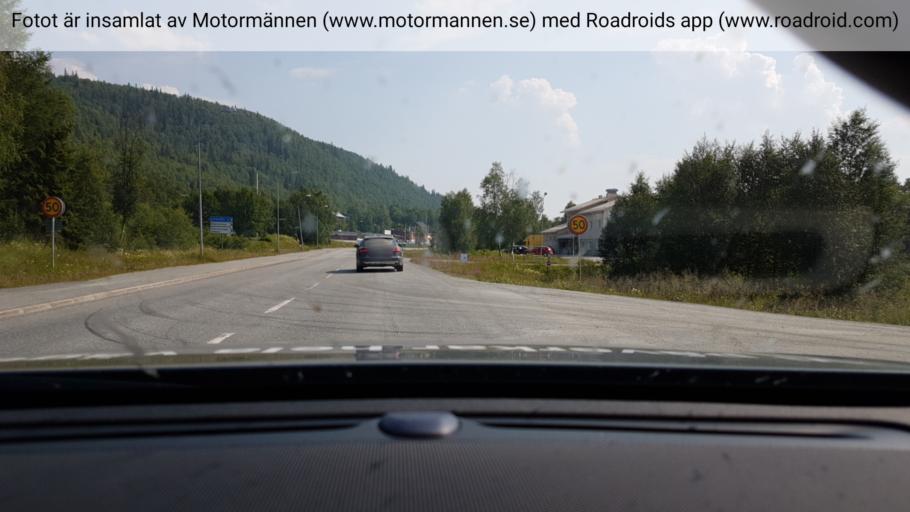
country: NO
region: Nordland
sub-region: Rana
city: Mo i Rana
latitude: 65.7119
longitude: 15.2309
